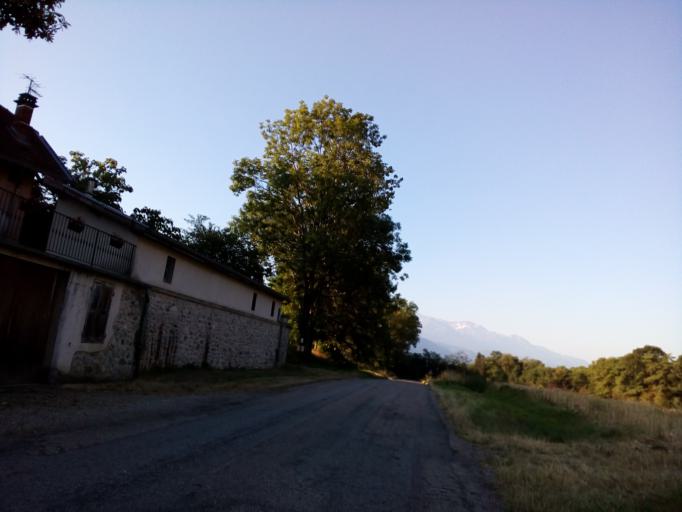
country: FR
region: Rhone-Alpes
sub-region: Departement de l'Isere
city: Barraux
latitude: 45.4255
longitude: 5.9817
